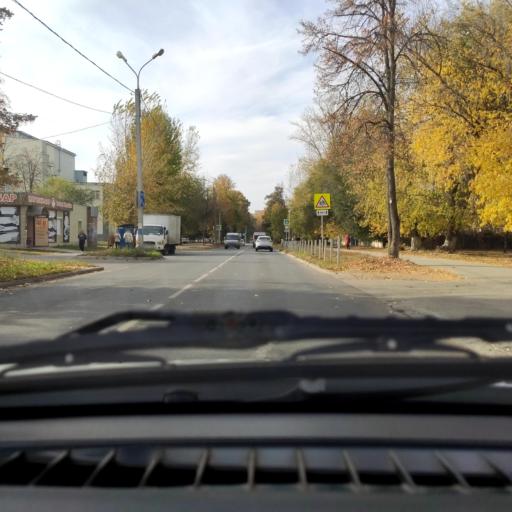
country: RU
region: Samara
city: Tol'yatti
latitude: 53.5053
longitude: 49.4028
